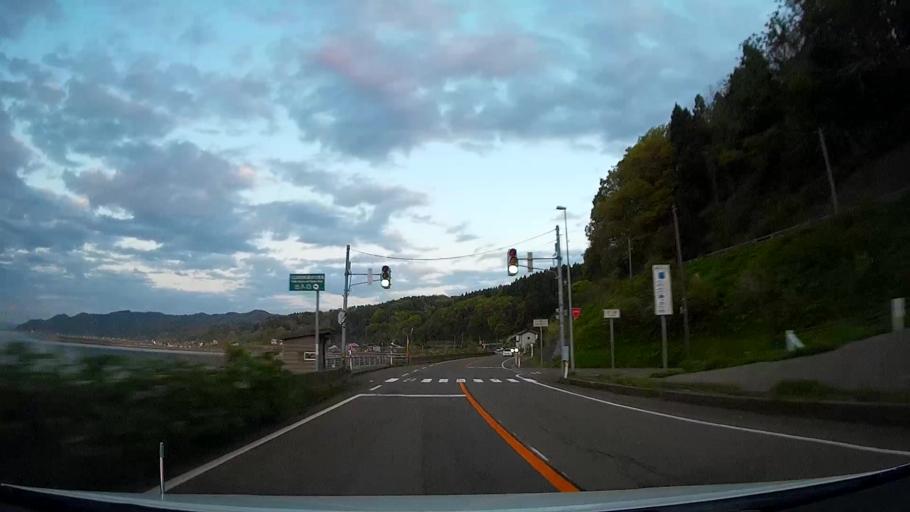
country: JP
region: Niigata
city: Joetsu
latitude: 37.1667
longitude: 138.1286
